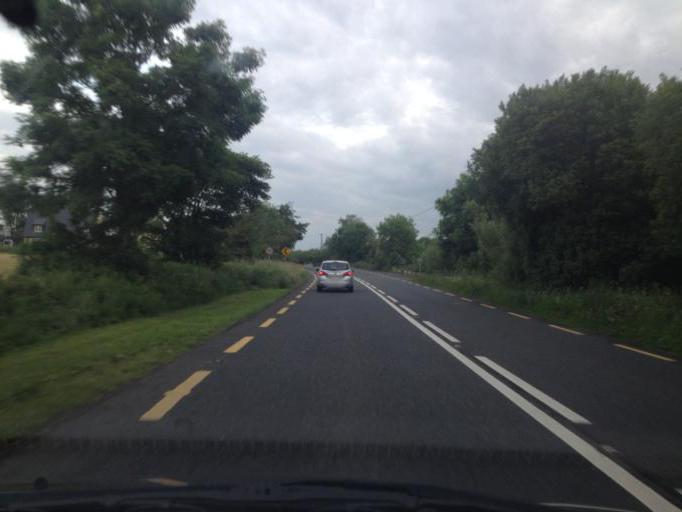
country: IE
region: Connaught
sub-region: Sligo
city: Sligo
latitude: 54.3448
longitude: -8.5040
